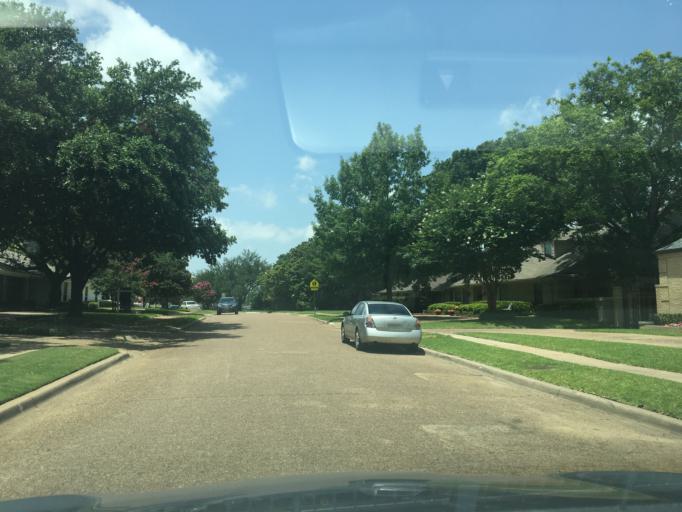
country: US
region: Texas
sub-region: Dallas County
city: University Park
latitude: 32.8844
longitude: -96.7810
